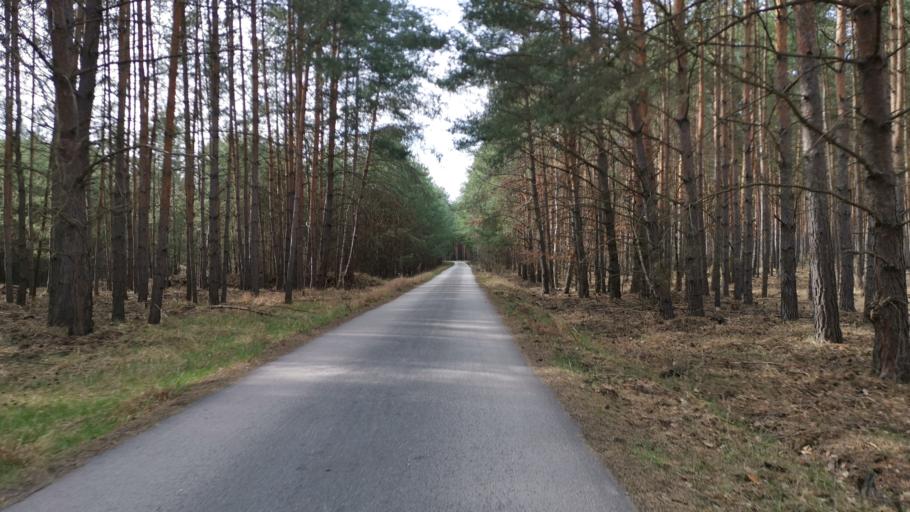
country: SK
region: Trnavsky
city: Gbely
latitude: 48.6867
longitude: 17.0625
